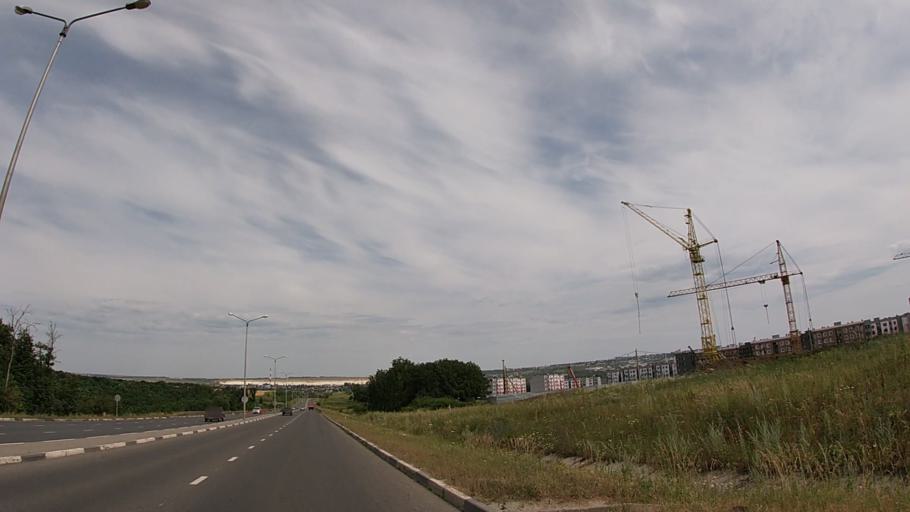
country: RU
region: Belgorod
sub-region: Belgorodskiy Rayon
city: Belgorod
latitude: 50.5960
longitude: 36.5307
